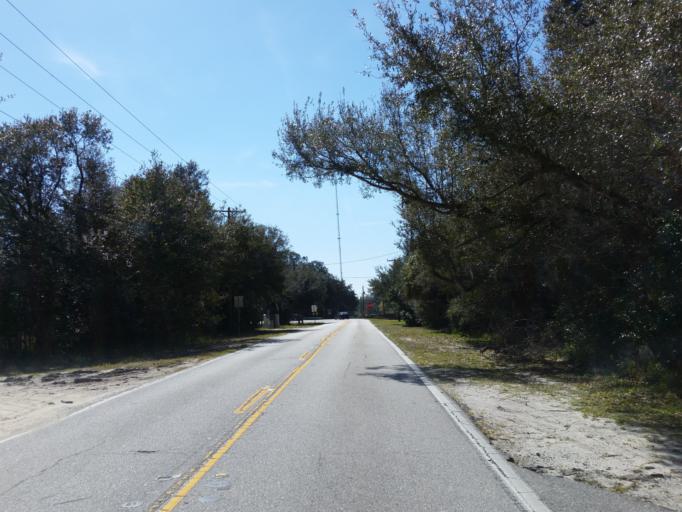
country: US
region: Florida
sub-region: Hillsborough County
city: Boyette
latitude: 27.8369
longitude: -82.2610
